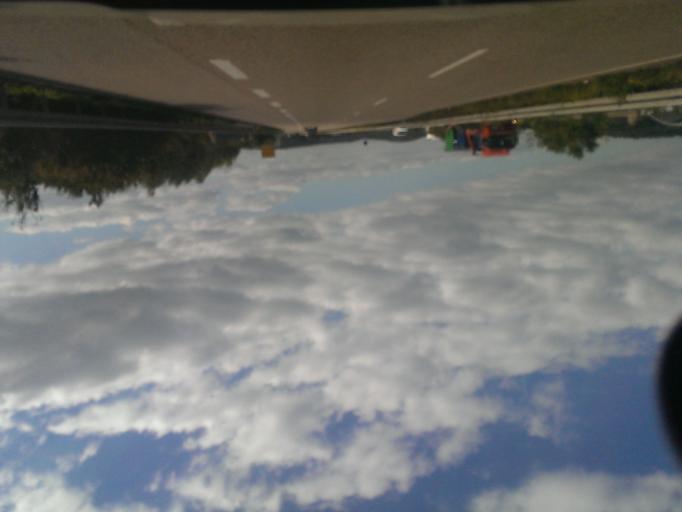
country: DE
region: Baden-Wuerttemberg
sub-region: Karlsruhe Region
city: Weingarten
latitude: 49.0138
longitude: 8.4726
